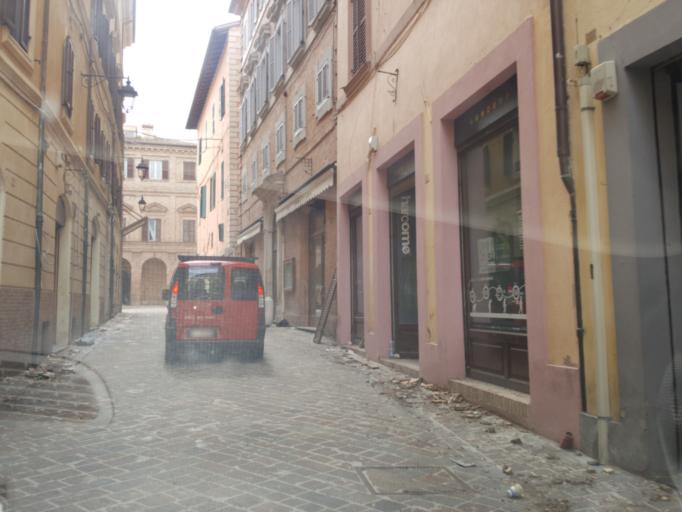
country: IT
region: The Marches
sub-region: Provincia di Macerata
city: Camerino
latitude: 43.1349
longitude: 13.0670
